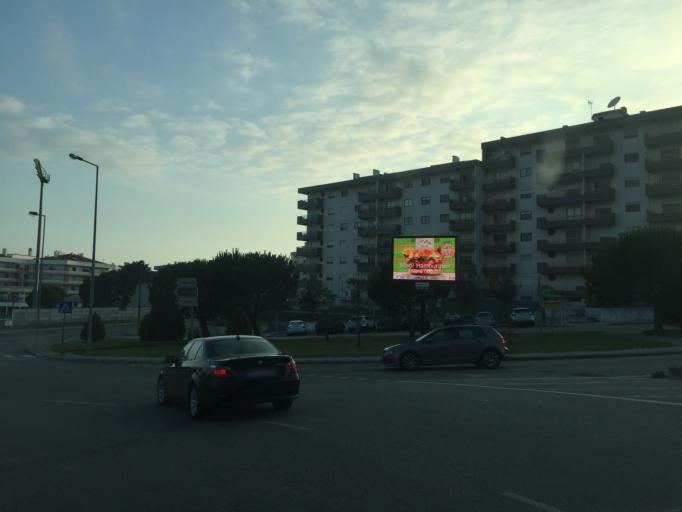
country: PT
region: Coimbra
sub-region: Figueira da Foz
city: Figueira da Foz
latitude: 40.1643
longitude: -8.8586
